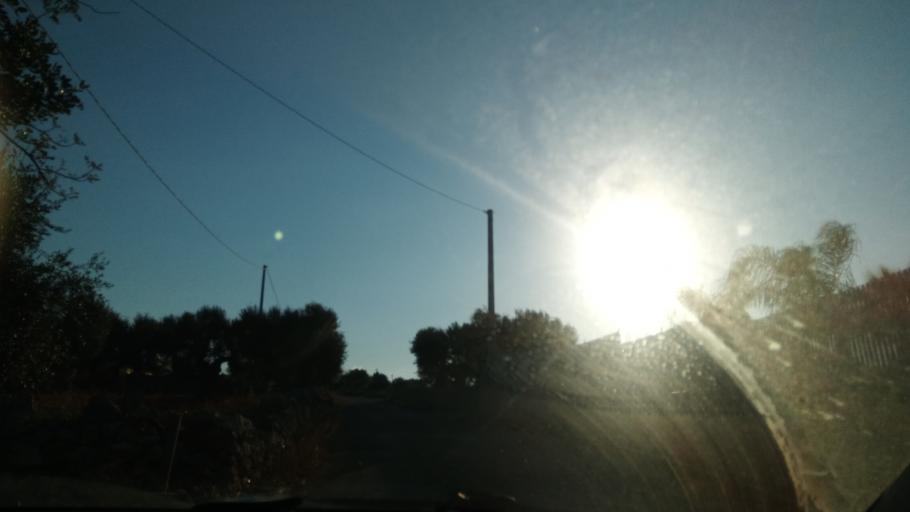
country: IT
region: Apulia
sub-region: Provincia di Bari
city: Polignano a Mare
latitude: 40.9823
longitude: 17.2088
